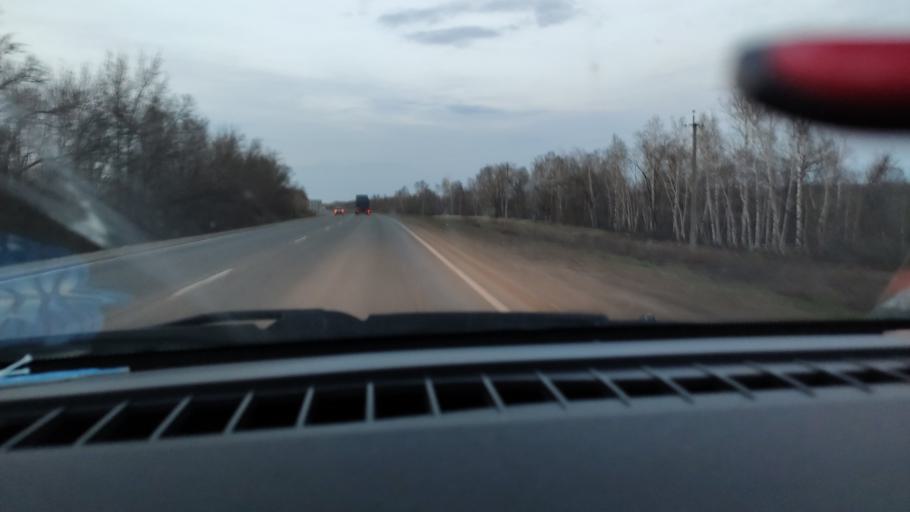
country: RU
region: Saratov
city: Sinodskoye
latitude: 52.0286
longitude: 46.7187
